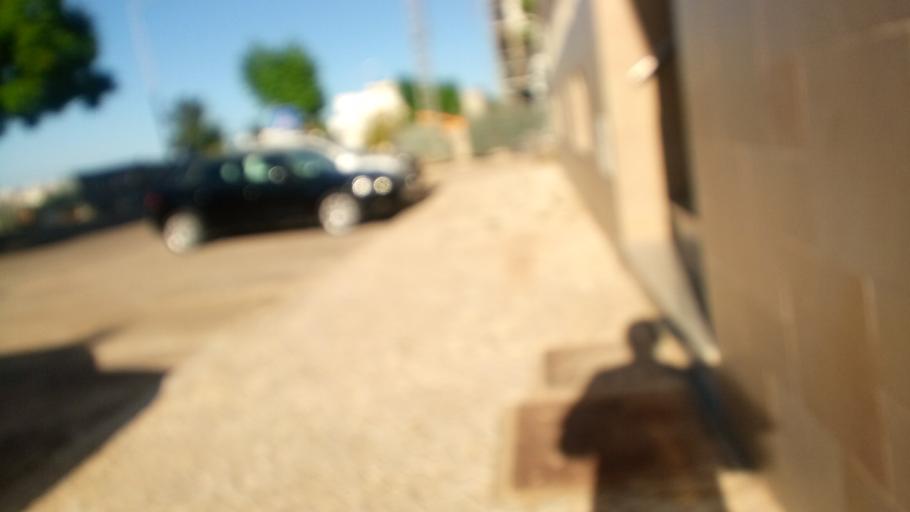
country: PT
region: Faro
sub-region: Tavira
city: Tavira
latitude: 37.1462
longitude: -7.6009
